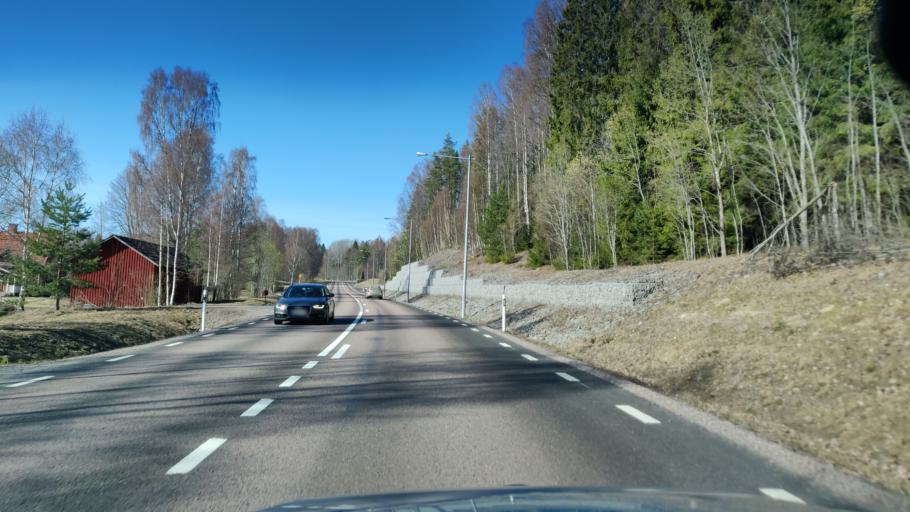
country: SE
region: Vaermland
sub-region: Hagfors Kommun
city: Hagfors
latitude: 59.9405
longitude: 13.6783
